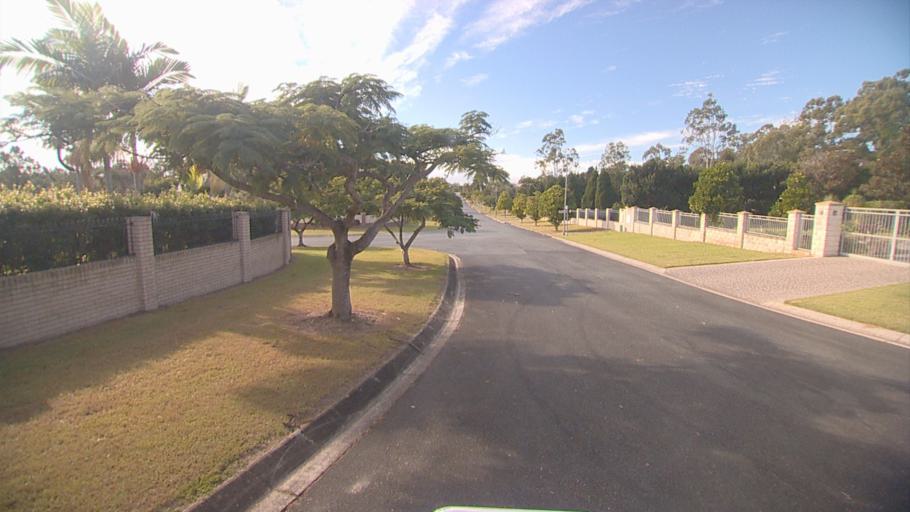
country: AU
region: Queensland
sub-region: Brisbane
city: Forest Lake
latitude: -27.6659
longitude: 153.0135
